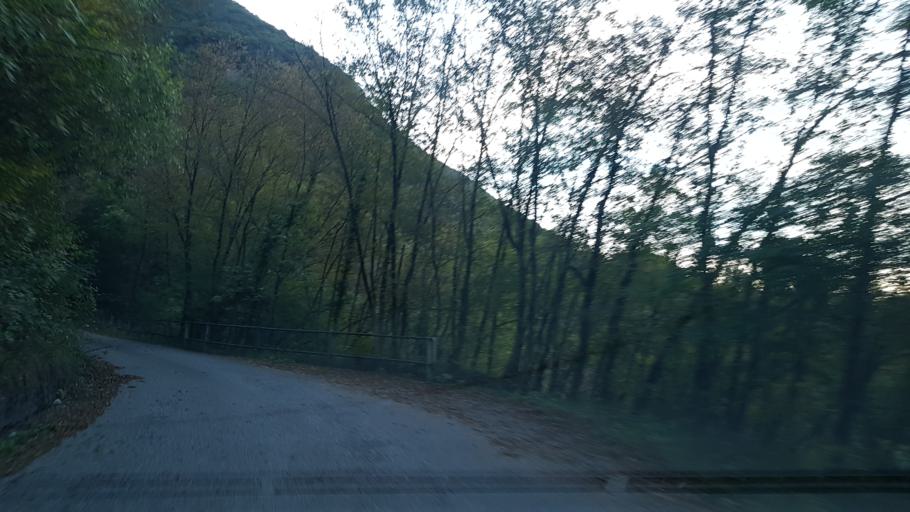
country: IT
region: Friuli Venezia Giulia
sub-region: Provincia di Udine
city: Venzone
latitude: 46.3354
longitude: 13.1707
